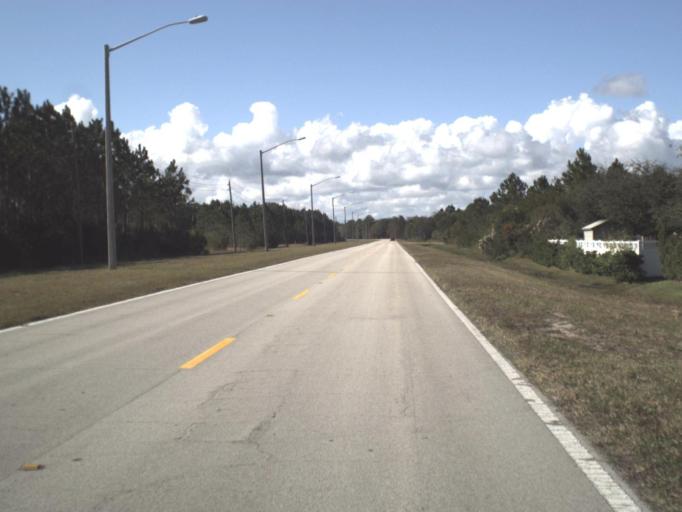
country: US
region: Florida
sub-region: Flagler County
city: Palm Coast
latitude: 29.6024
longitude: -81.2689
